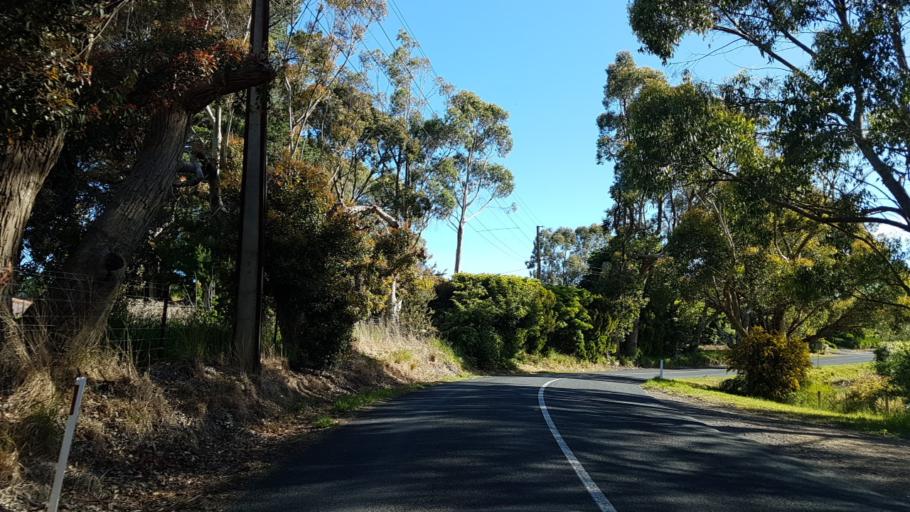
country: AU
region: South Australia
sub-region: Adelaide Hills
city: Adelaide Hills
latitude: -34.9381
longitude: 138.7413
